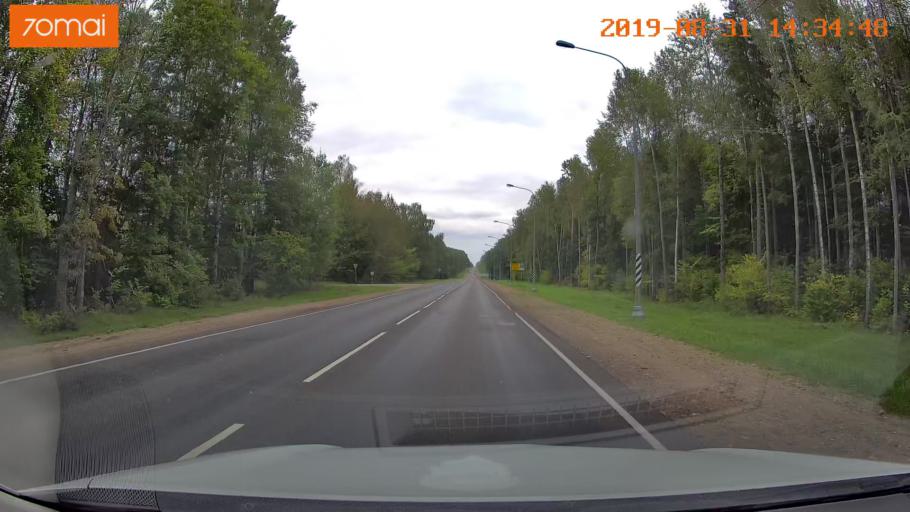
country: RU
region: Smolensk
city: Yekimovichi
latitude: 54.1593
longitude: 33.4440
